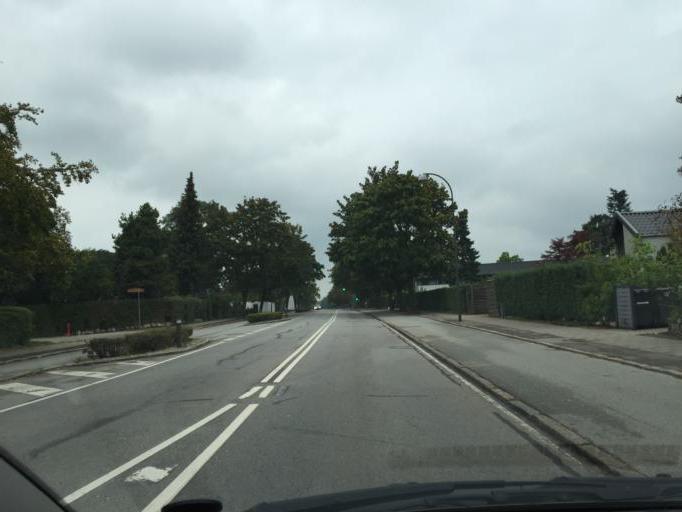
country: DK
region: Capital Region
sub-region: Herlev Kommune
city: Herlev
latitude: 55.7356
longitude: 12.4335
